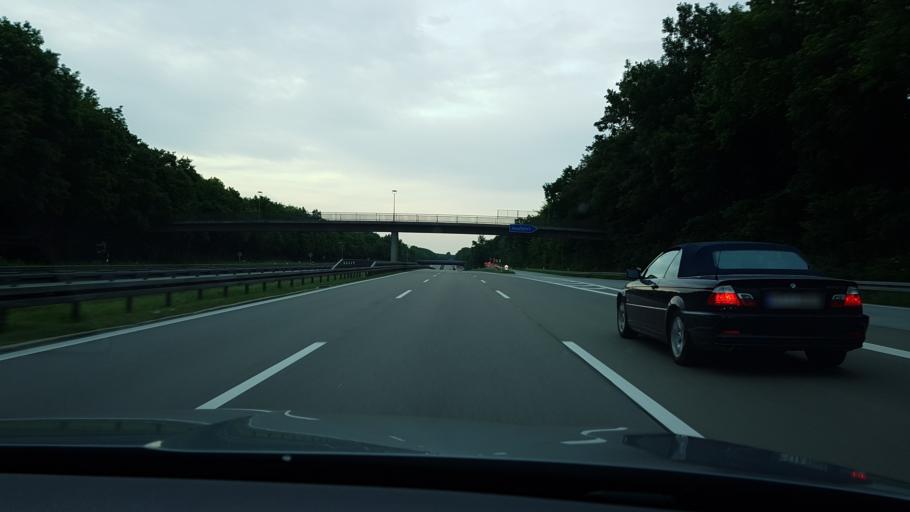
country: DE
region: Bavaria
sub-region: Upper Bavaria
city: Neuried
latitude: 48.0807
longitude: 11.4881
